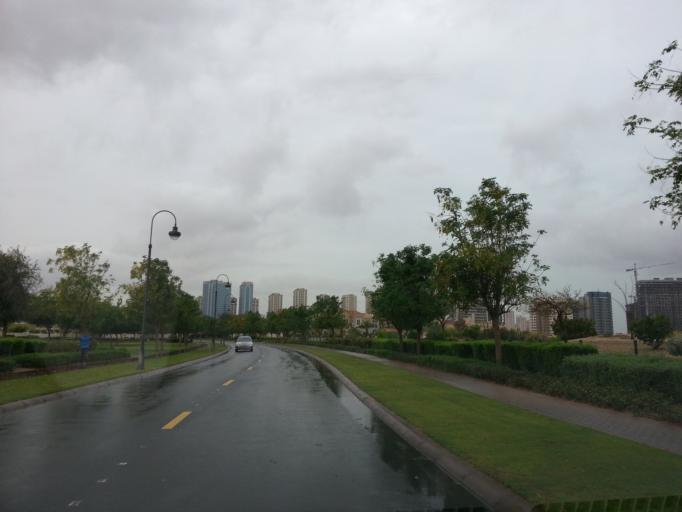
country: AE
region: Dubai
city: Dubai
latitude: 25.0369
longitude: 55.2127
